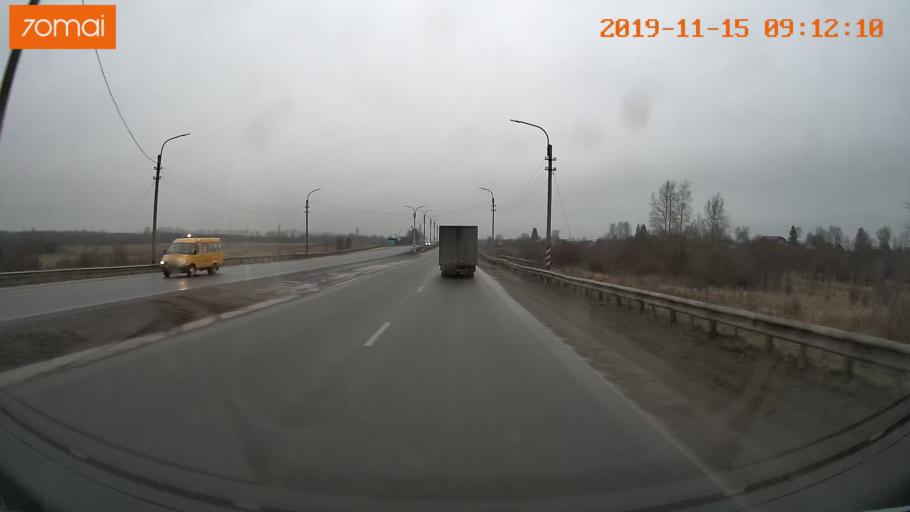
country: RU
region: Vologda
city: Tonshalovo
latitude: 59.2051
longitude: 37.9398
